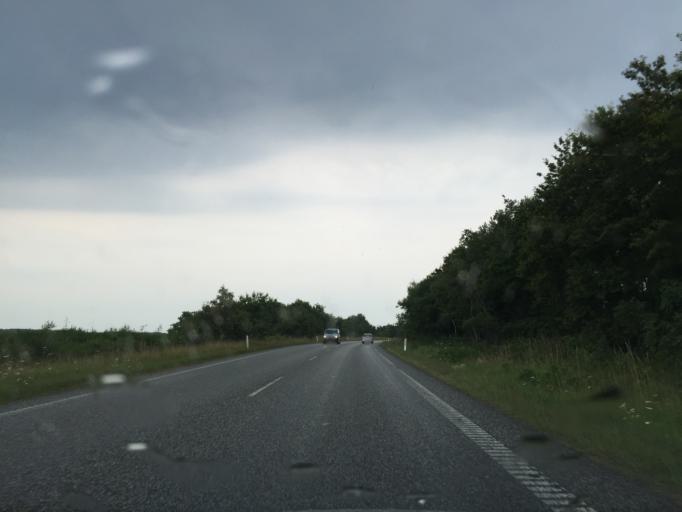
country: DK
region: Central Jutland
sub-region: Viborg Kommune
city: Bjerringbro
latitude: 56.3039
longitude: 9.6526
